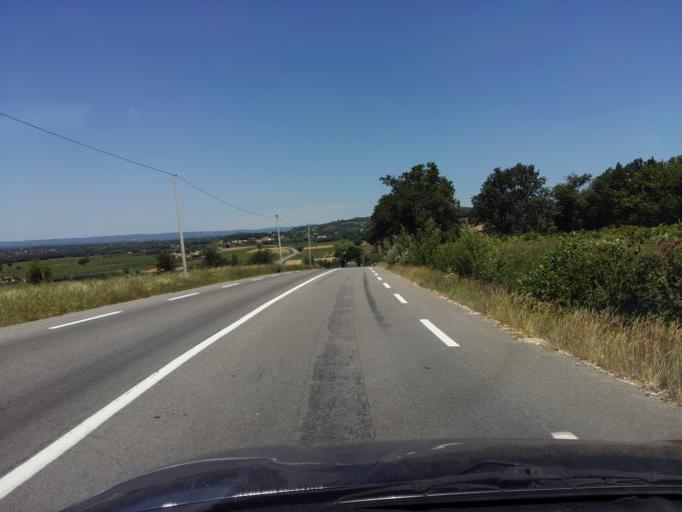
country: FR
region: Rhone-Alpes
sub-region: Departement de la Drome
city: Tulette
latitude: 44.2926
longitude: 4.9426
